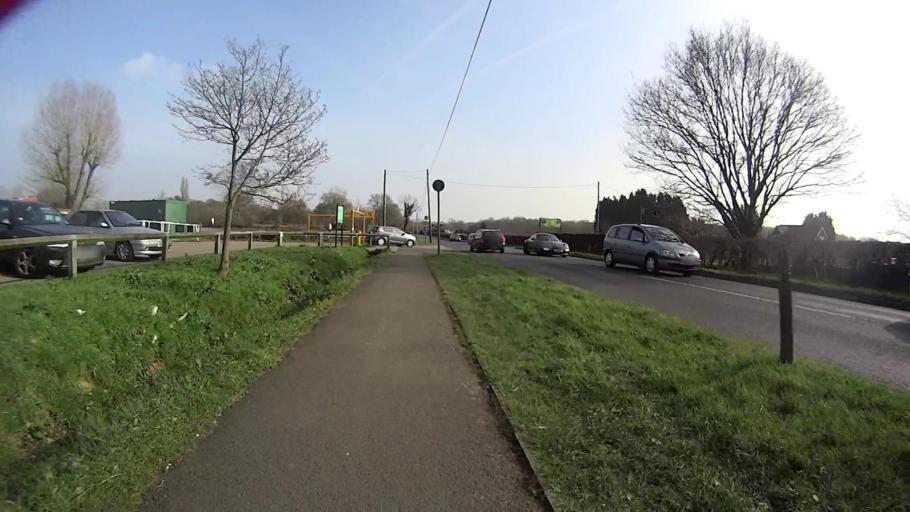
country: GB
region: England
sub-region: Surrey
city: Salfords
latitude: 51.2204
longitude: -0.1860
